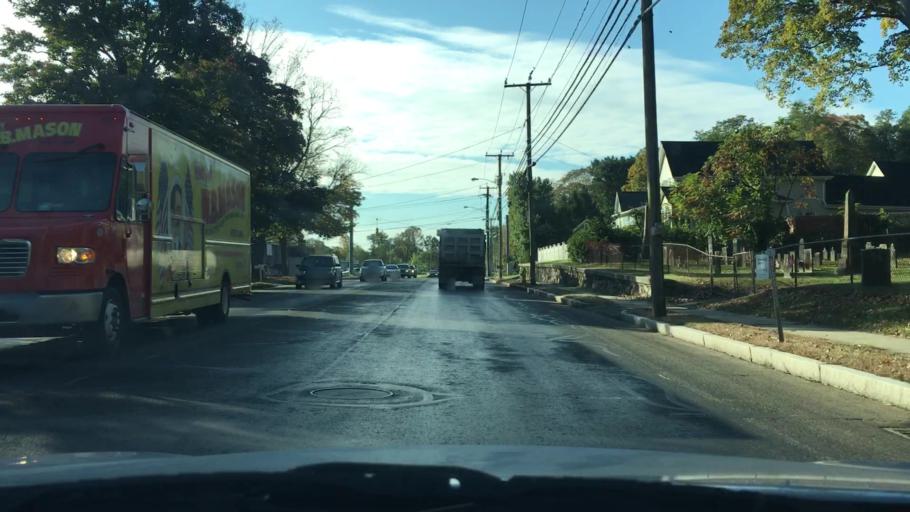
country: US
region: Massachusetts
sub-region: Hampden County
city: Agawam
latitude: 42.0614
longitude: -72.6762
